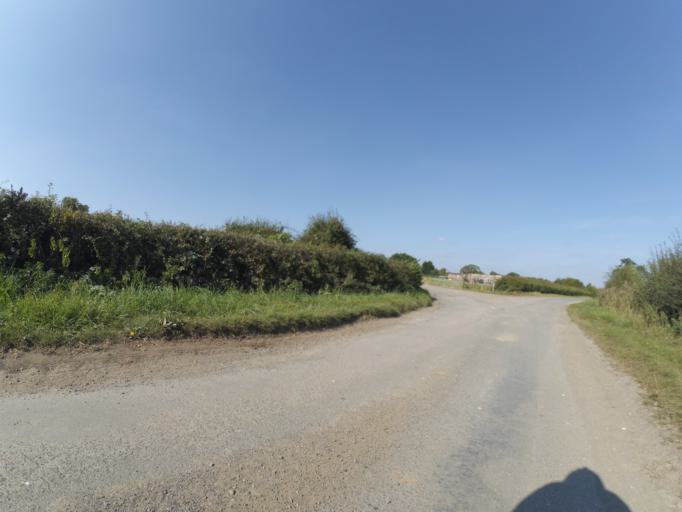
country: GB
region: England
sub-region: Warwickshire
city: Rugby
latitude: 52.4053
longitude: -1.2668
